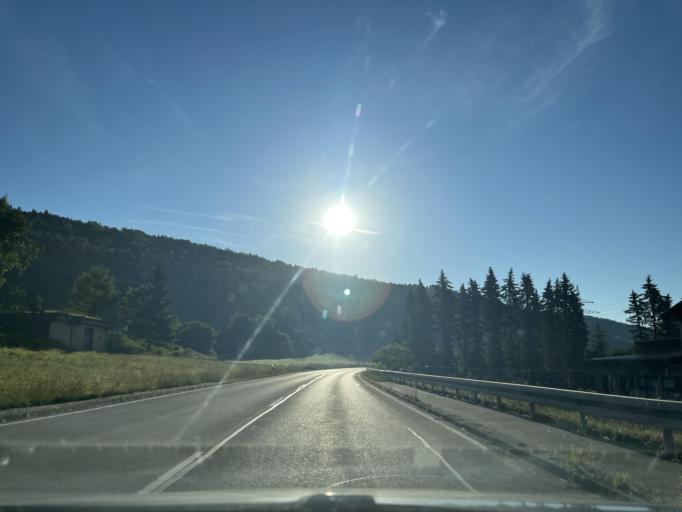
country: DE
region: Baden-Wuerttemberg
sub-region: Tuebingen Region
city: Burladingen
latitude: 48.2897
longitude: 9.1406
